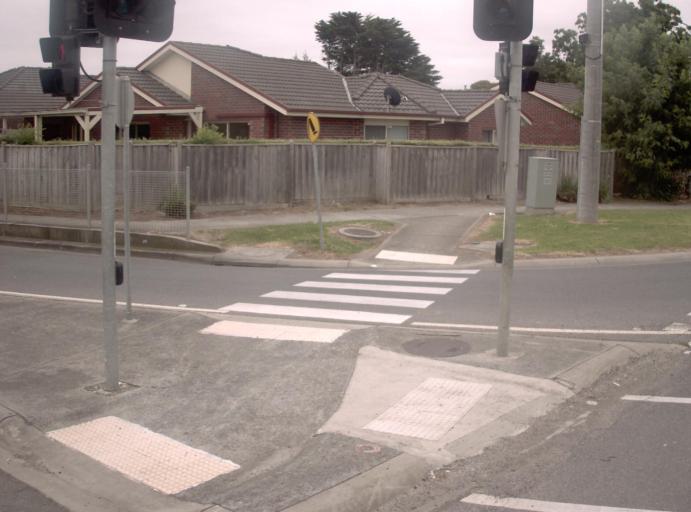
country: AU
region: Victoria
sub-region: Casey
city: Hallam
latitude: -38.0016
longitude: 145.2742
